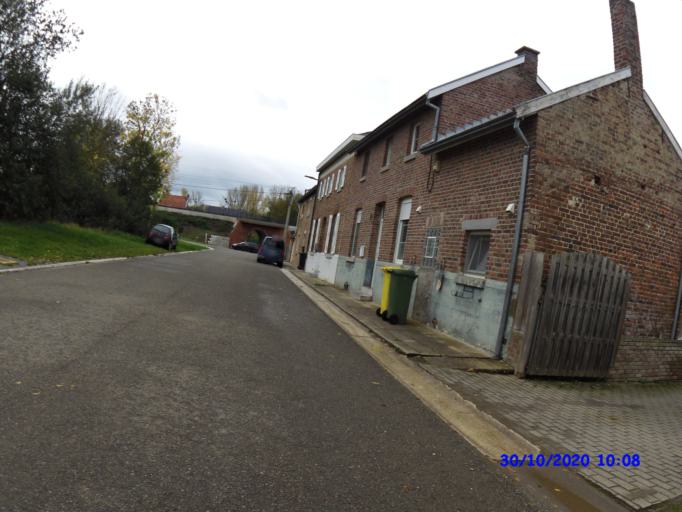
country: BE
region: Wallonia
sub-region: Province de Liege
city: Berloz
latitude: 50.7030
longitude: 5.2216
